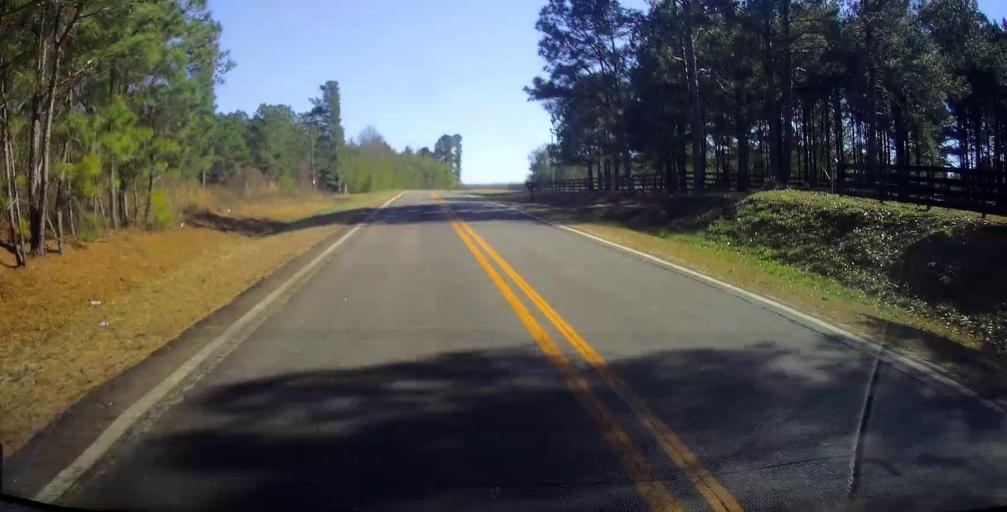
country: US
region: Georgia
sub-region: Crawford County
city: Knoxville
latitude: 32.6209
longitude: -83.9873
